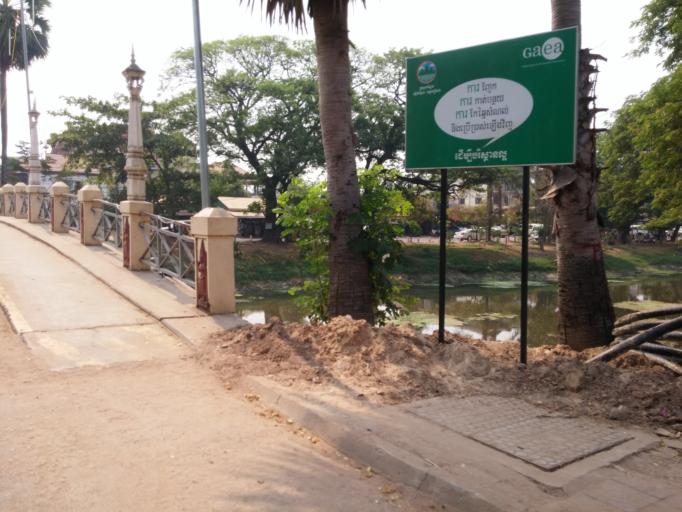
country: KH
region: Siem Reap
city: Siem Reap
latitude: 13.3639
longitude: 103.8611
